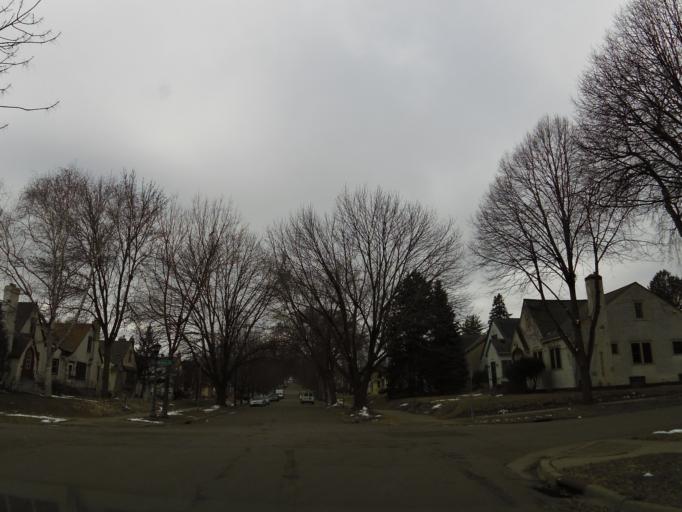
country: US
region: Minnesota
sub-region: Dakota County
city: Mendota Heights
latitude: 44.9254
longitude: -93.1645
